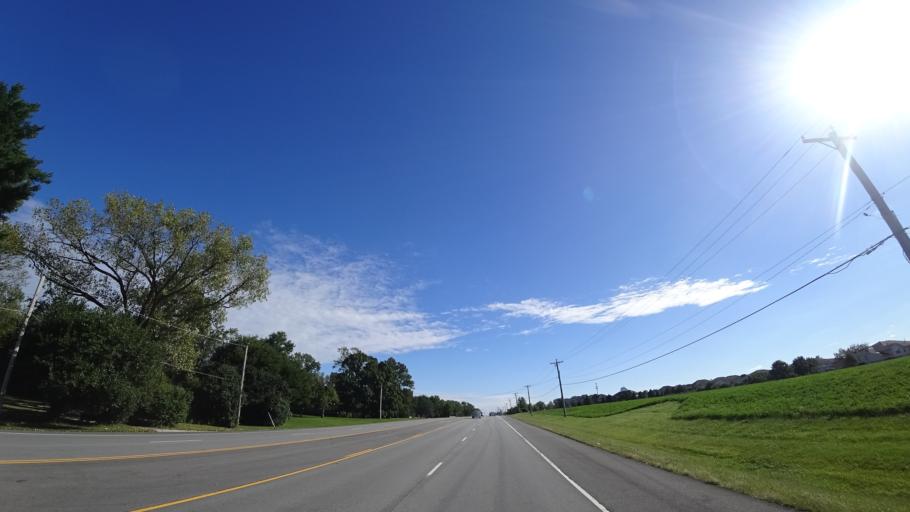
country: US
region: Illinois
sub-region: Cook County
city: Country Club Hills
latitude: 41.5639
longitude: -87.7333
